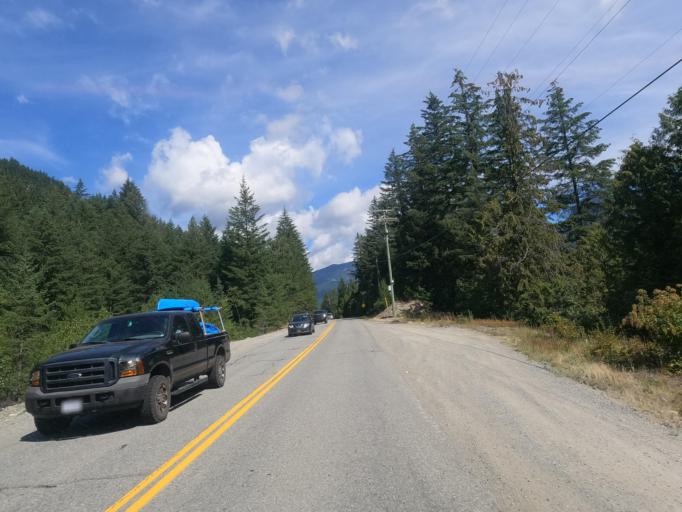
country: CA
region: British Columbia
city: Pemberton
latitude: 50.3230
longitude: -122.7213
